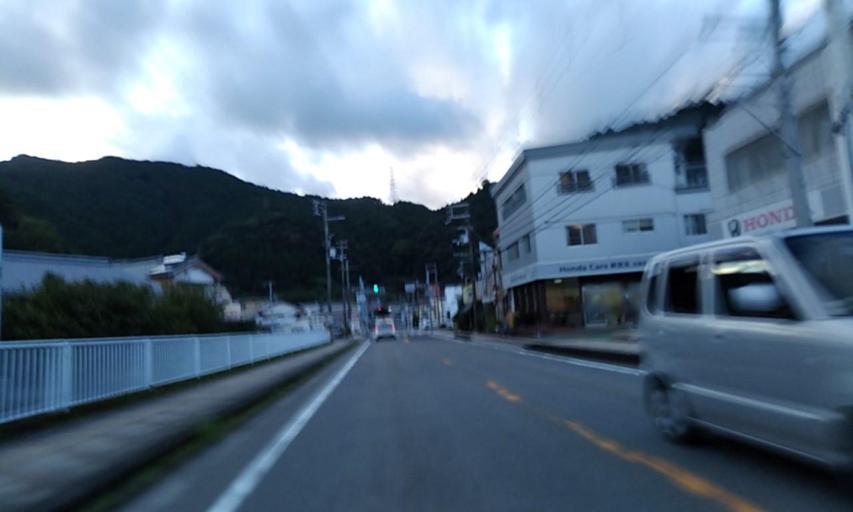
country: JP
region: Wakayama
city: Shingu
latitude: 33.7189
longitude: 135.9838
